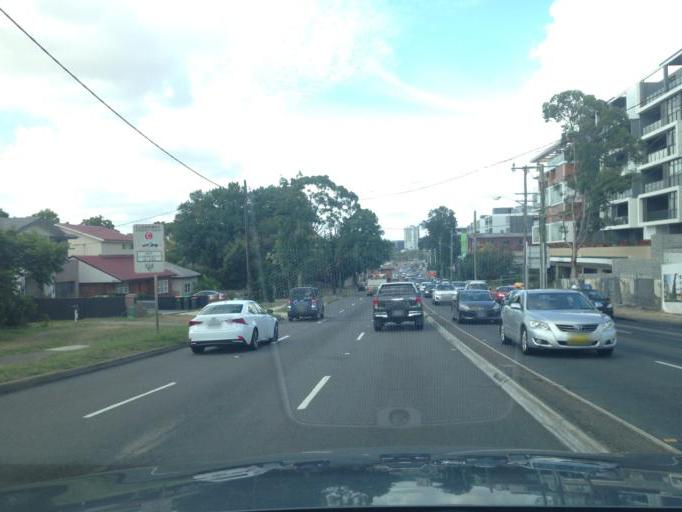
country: AU
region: New South Wales
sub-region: Canada Bay
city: Rhodes
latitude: -33.8196
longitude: 151.0996
